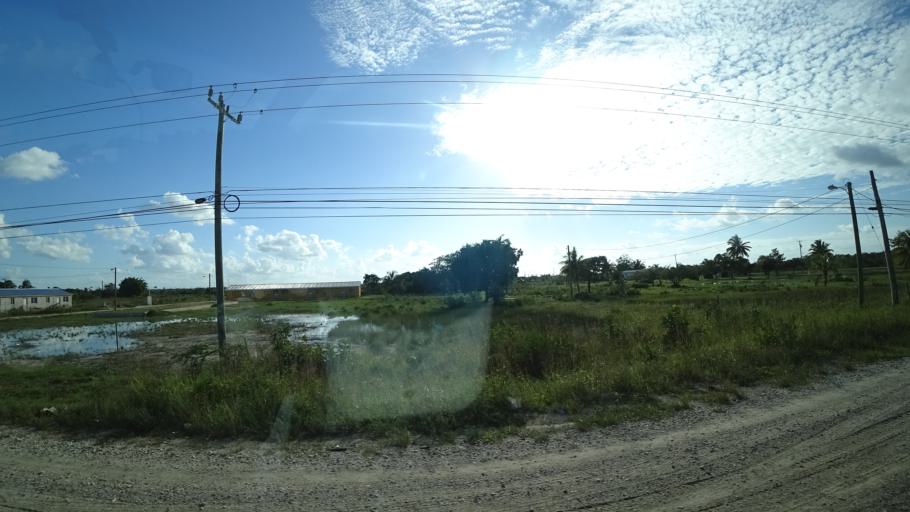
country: BZ
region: Belize
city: Belize City
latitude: 17.5673
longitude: -88.3292
